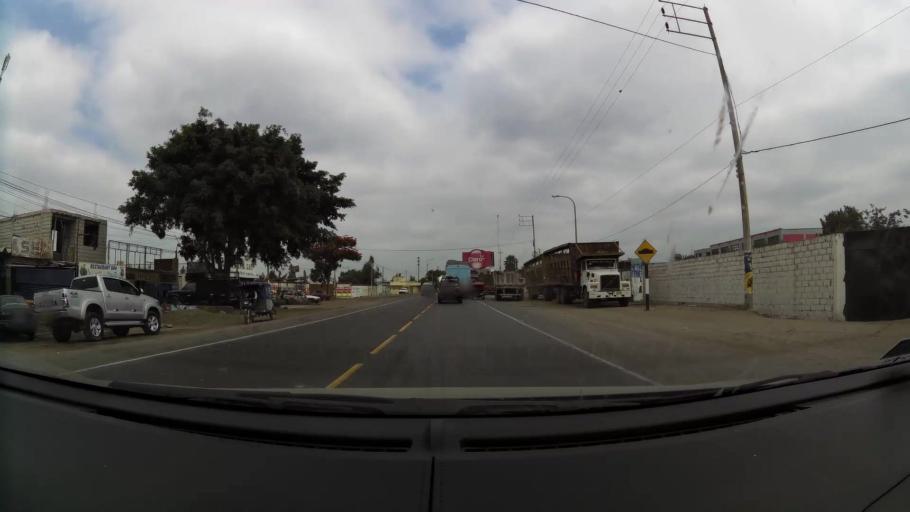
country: PE
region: La Libertad
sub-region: Ascope
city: Chocope
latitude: -7.7934
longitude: -79.2201
